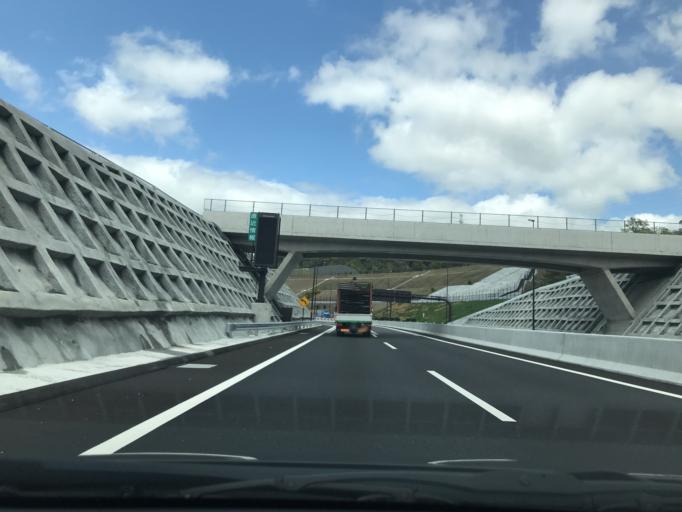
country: JP
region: Osaka
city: Takatsuki
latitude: 34.8828
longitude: 135.6259
